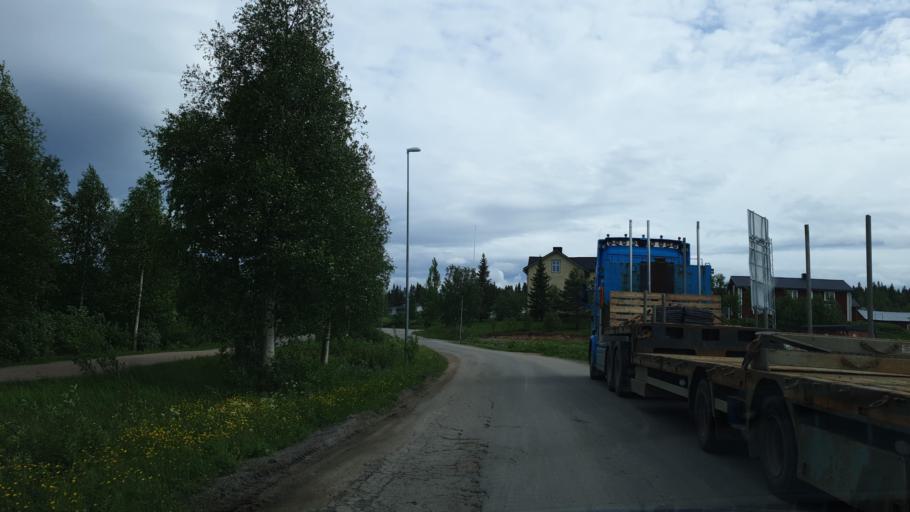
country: SE
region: Norrbotten
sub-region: Gallivare Kommun
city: Gaellivare
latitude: 67.1287
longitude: 20.6495
